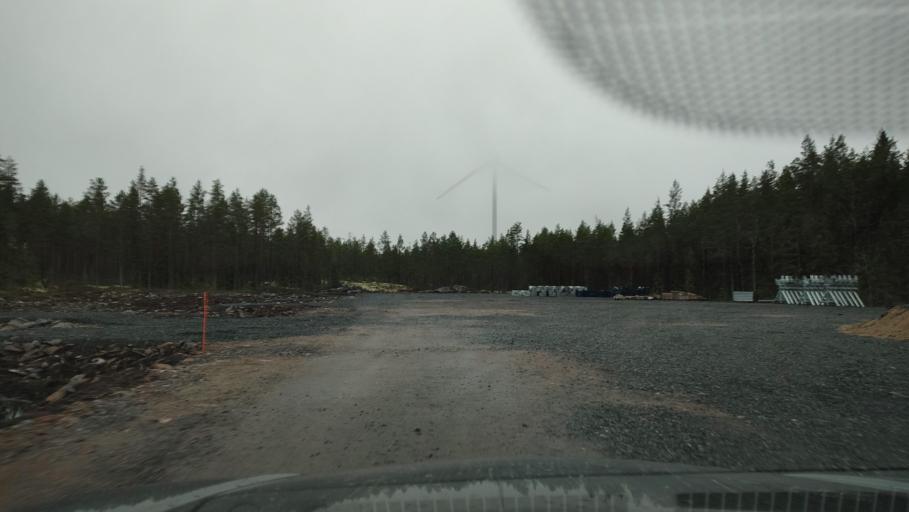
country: FI
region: Southern Ostrobothnia
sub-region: Suupohja
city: Karijoki
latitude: 62.1606
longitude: 21.6104
